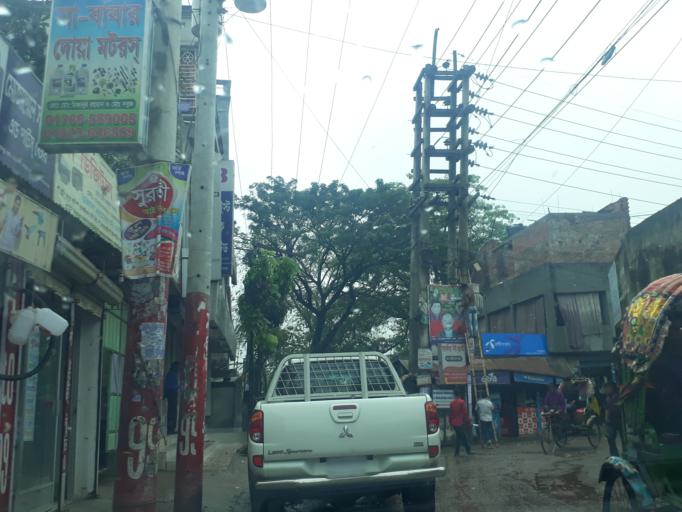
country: BD
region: Dhaka
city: Tungi
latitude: 23.8972
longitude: 90.3308
